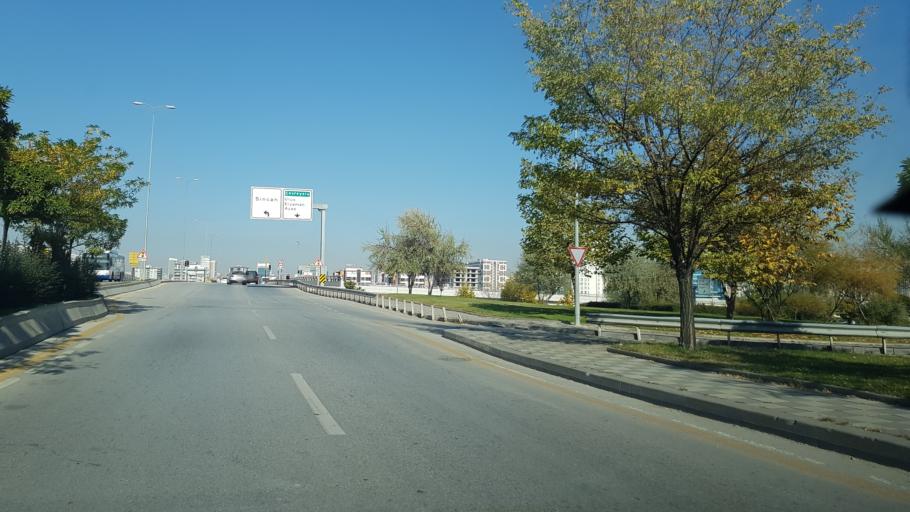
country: TR
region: Ankara
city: Etimesgut
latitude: 39.9588
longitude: 32.6052
